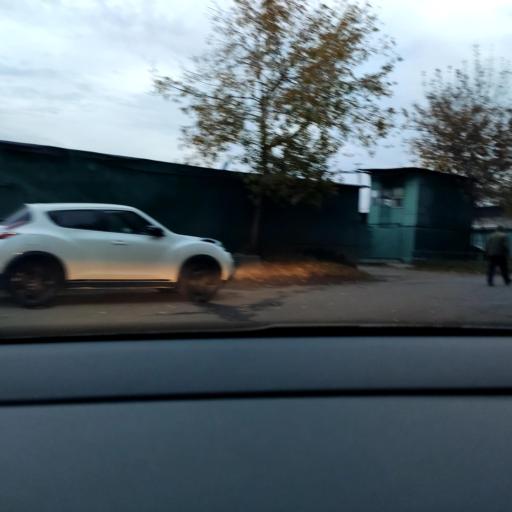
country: RU
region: Moscow
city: Bibirevo
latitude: 55.8832
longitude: 37.6083
